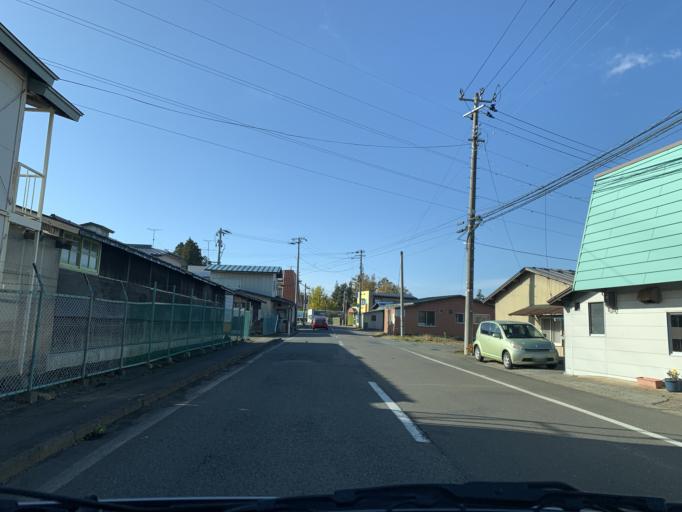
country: JP
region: Iwate
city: Kitakami
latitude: 39.2312
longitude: 141.0876
